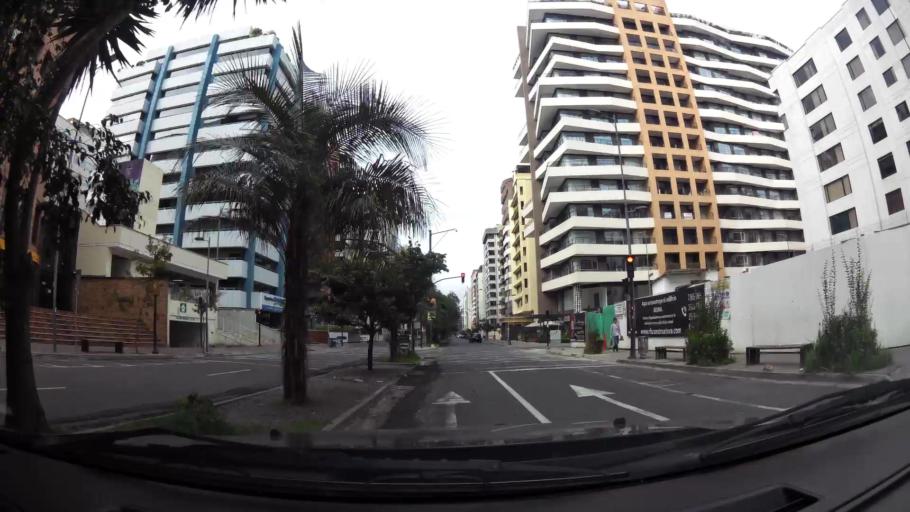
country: EC
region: Pichincha
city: Quito
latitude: -0.1794
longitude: -78.4800
